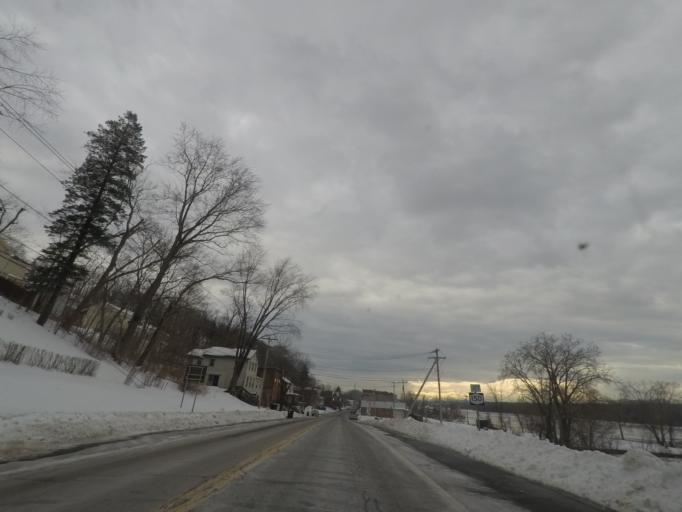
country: US
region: New York
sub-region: Rensselaer County
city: Castleton-on-Hudson
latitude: 42.5326
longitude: -73.7559
